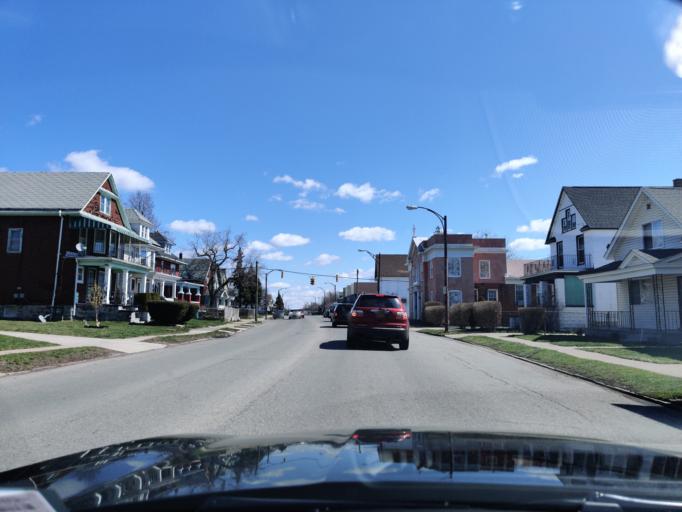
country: US
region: New York
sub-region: Erie County
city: Sloan
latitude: 42.9217
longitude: -78.8345
